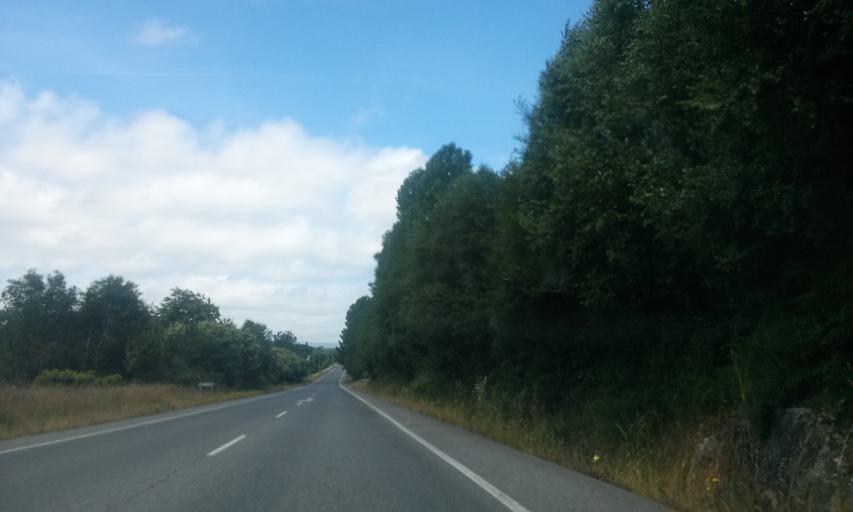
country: ES
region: Galicia
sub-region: Provincia de Lugo
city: Friol
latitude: 43.0307
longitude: -7.7037
